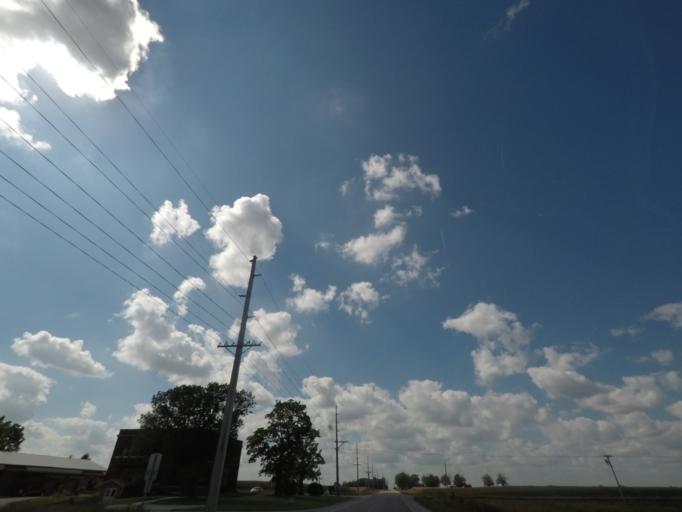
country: US
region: Iowa
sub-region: Story County
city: Ames
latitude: 42.0231
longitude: -93.5395
